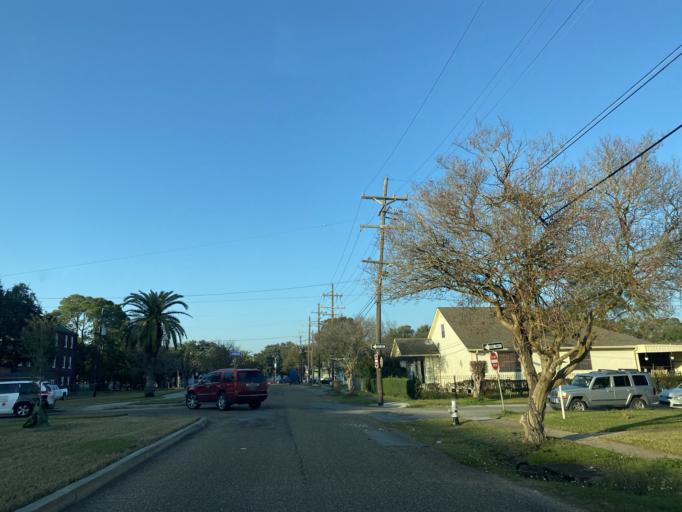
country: US
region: Louisiana
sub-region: Orleans Parish
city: New Orleans
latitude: 29.9934
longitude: -90.0634
